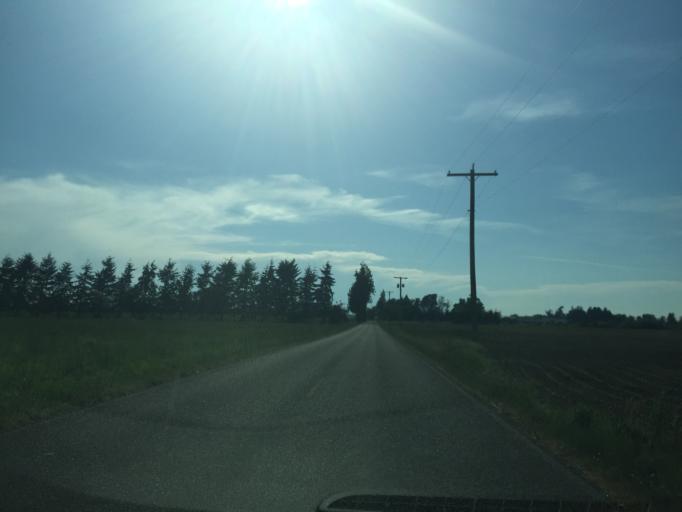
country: US
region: Washington
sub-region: Whatcom County
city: Lynden
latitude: 48.9970
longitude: -122.4546
